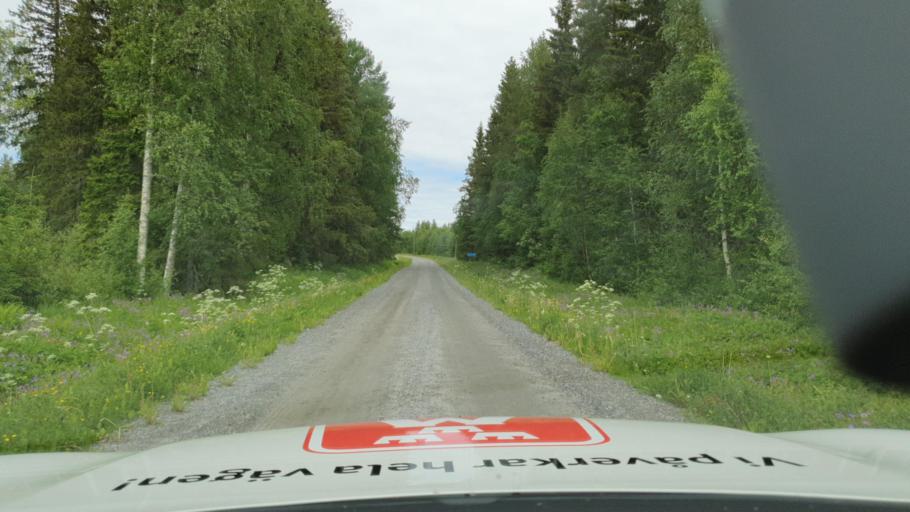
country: SE
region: Vaesterbotten
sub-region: Skelleftea Kommun
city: Langsele
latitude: 64.4741
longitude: 20.2632
